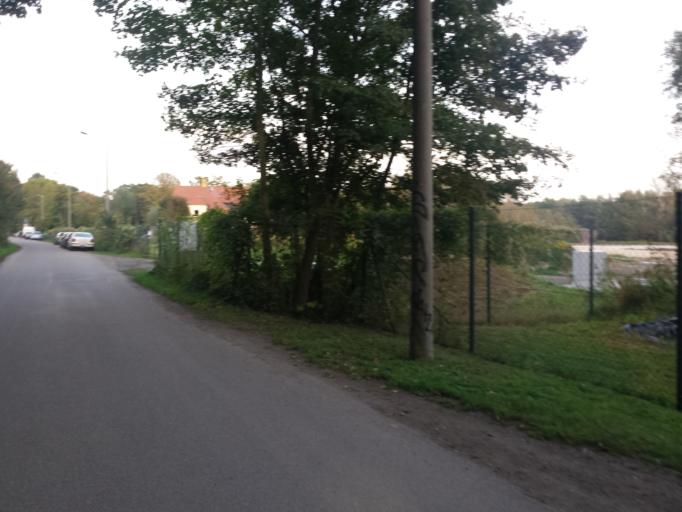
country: DE
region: Saxony
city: Markkleeberg
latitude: 51.2929
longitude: 12.3790
